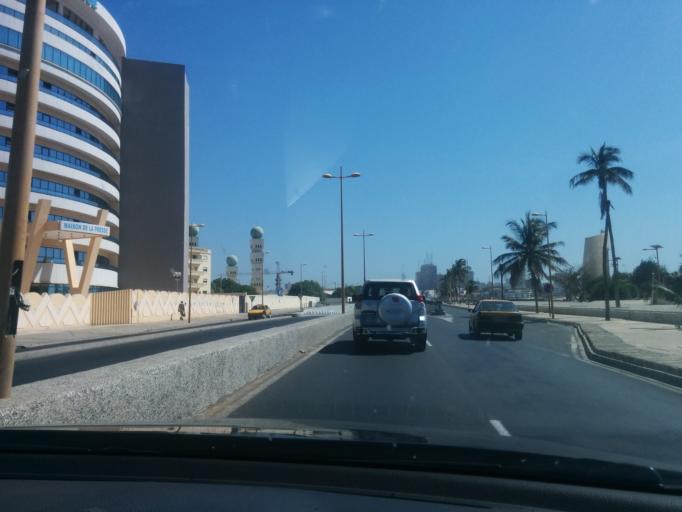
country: SN
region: Dakar
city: Dakar
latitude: 14.6740
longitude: -17.4515
